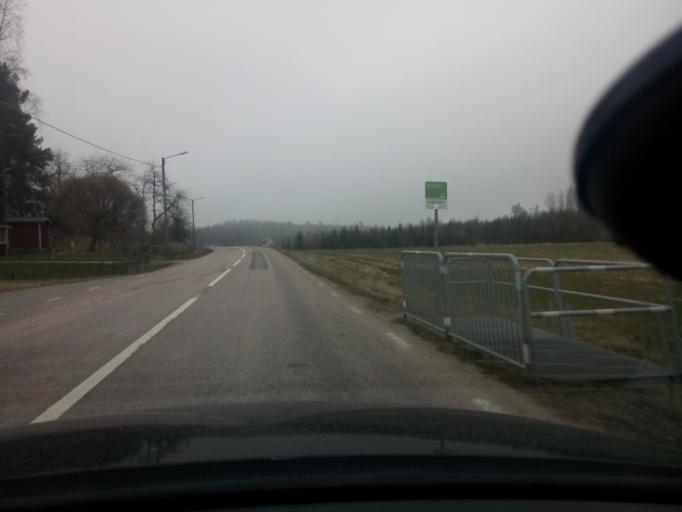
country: SE
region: Soedermanland
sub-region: Nykopings Kommun
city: Nykoping
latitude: 58.9182
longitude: 17.0962
